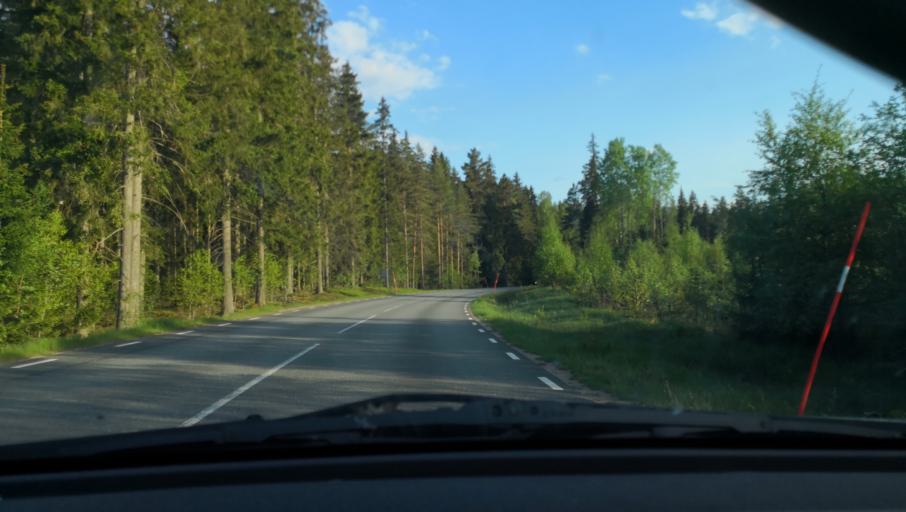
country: SE
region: Joenkoeping
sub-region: Vetlanda Kommun
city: Landsbro
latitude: 57.3907
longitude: 14.8274
